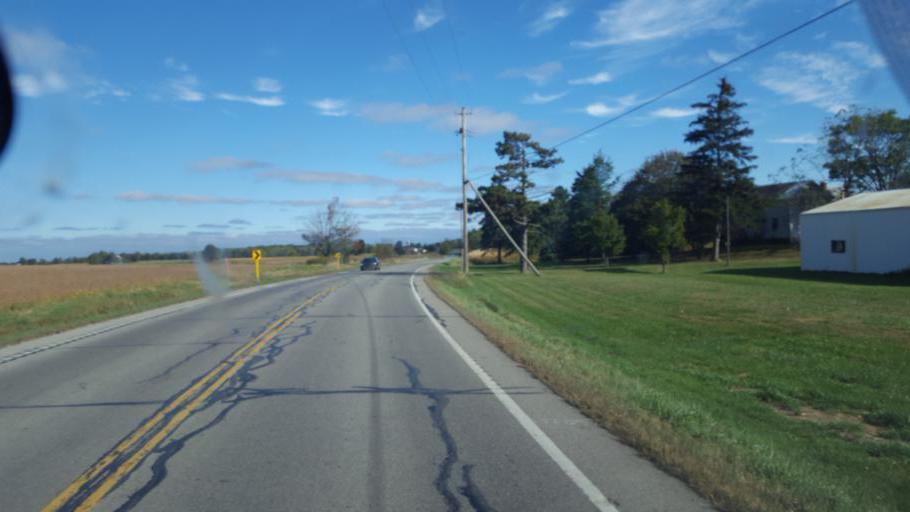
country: US
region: Ohio
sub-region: Huron County
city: Greenwich
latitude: 40.9684
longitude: -82.4955
